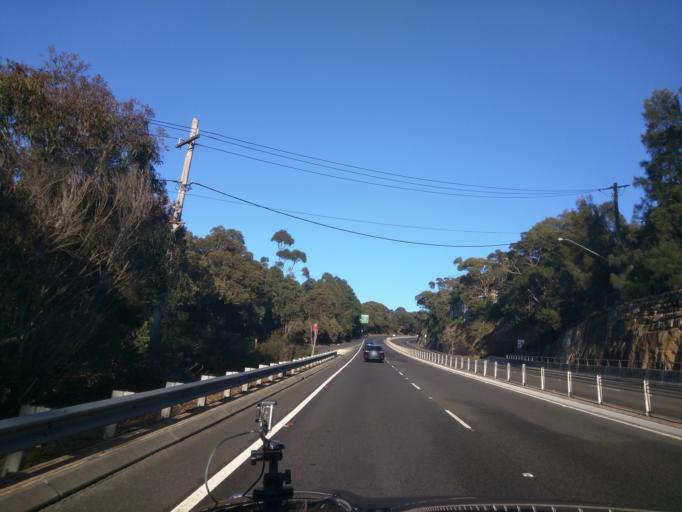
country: AU
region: New South Wales
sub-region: Sutherland Shire
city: Bonnet Bay
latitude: -34.0200
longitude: 151.0445
